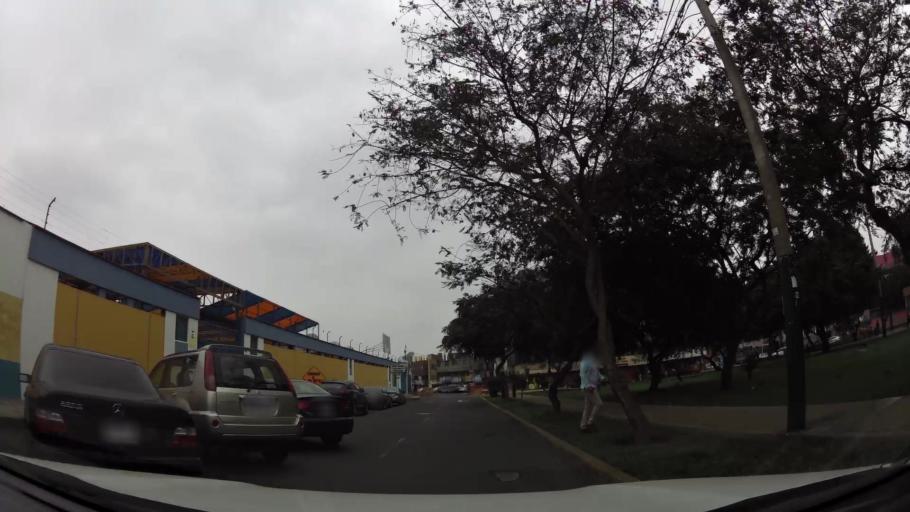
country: PE
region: Lima
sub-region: Lima
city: Surco
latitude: -12.1272
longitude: -76.9992
